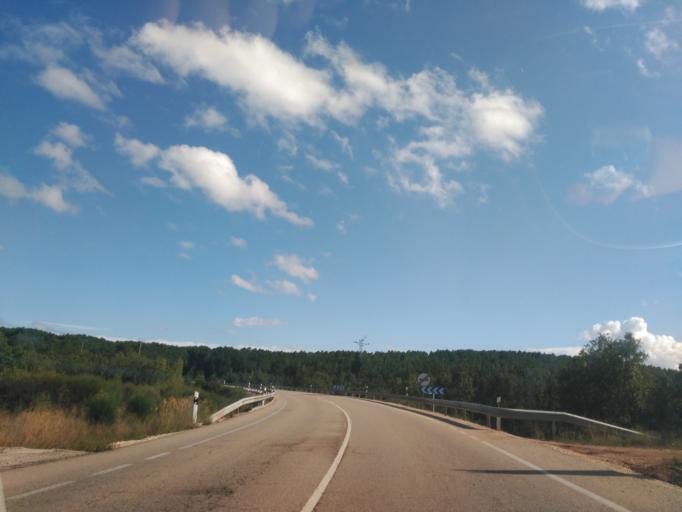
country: ES
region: Castille and Leon
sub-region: Provincia de Burgos
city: Pinilla de los Barruecos
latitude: 41.9158
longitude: -3.2793
